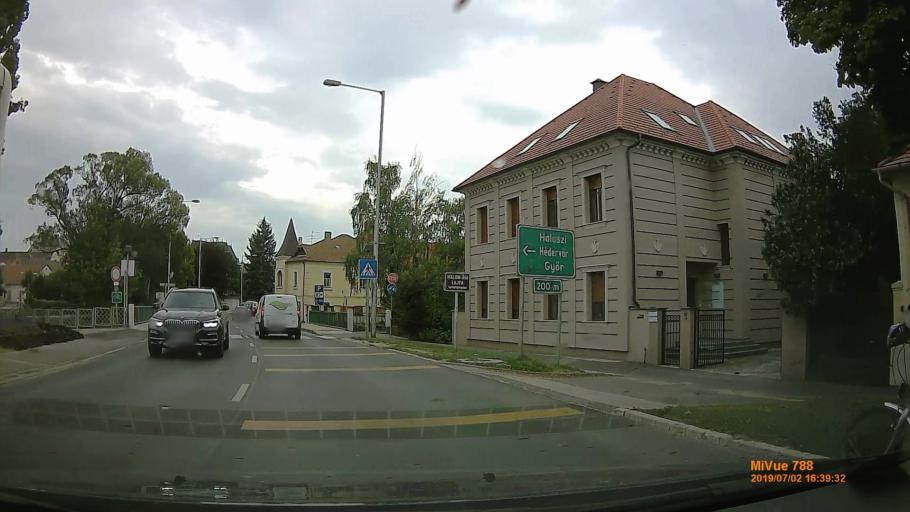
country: HU
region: Gyor-Moson-Sopron
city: Mosonmagyarovar
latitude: 47.8803
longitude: 17.2718
